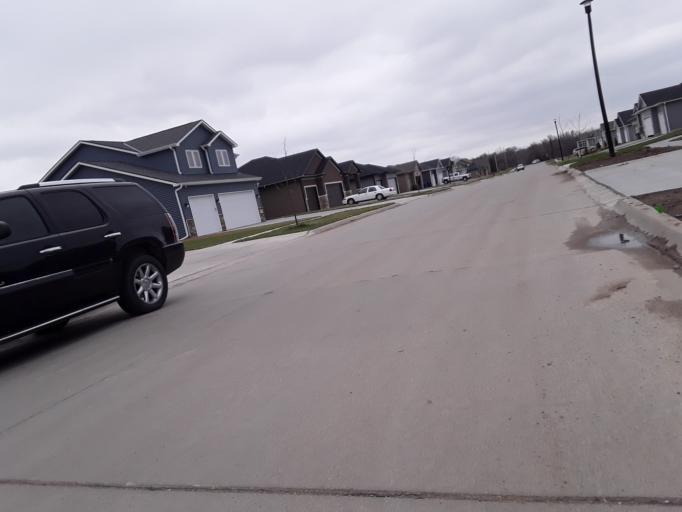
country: US
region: Nebraska
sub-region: Lancaster County
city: Lincoln
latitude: 40.8451
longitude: -96.5935
